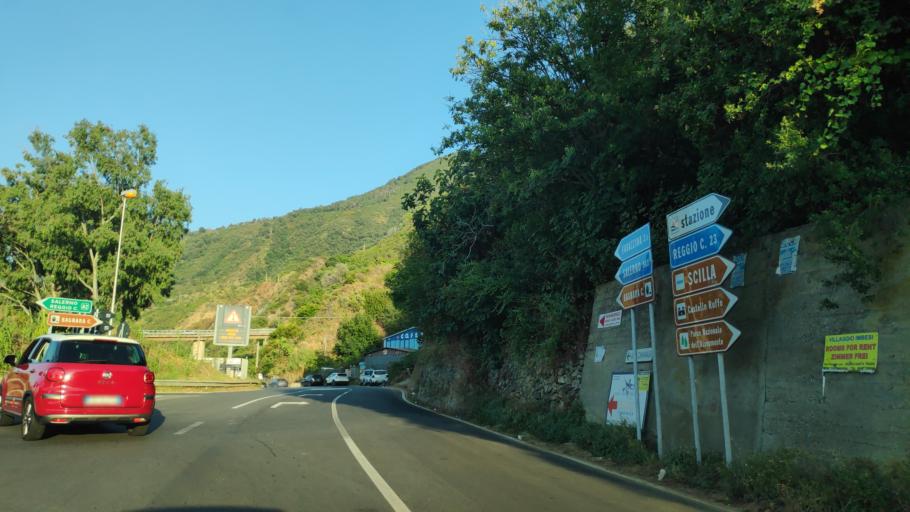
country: IT
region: Calabria
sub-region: Provincia di Reggio Calabria
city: Scilla
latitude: 38.2533
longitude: 15.7258
